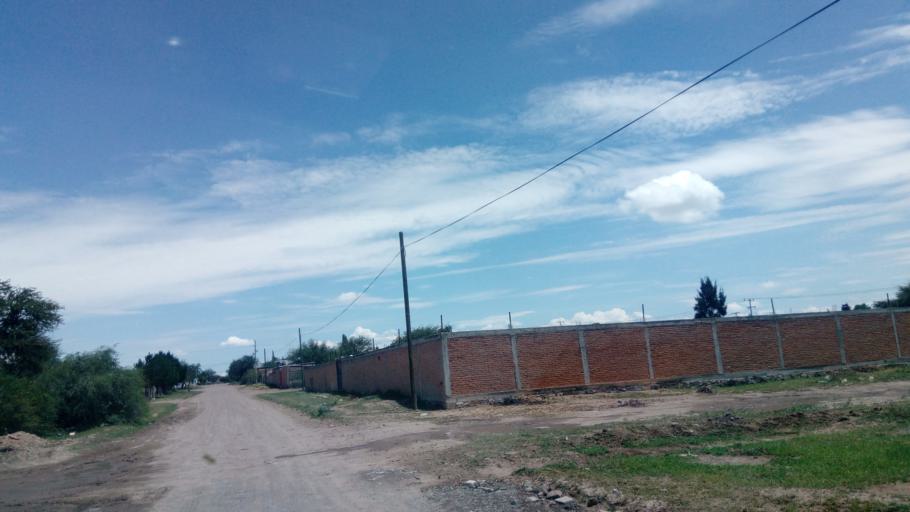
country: MX
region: Durango
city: Victoria de Durango
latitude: 24.0150
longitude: -104.5908
